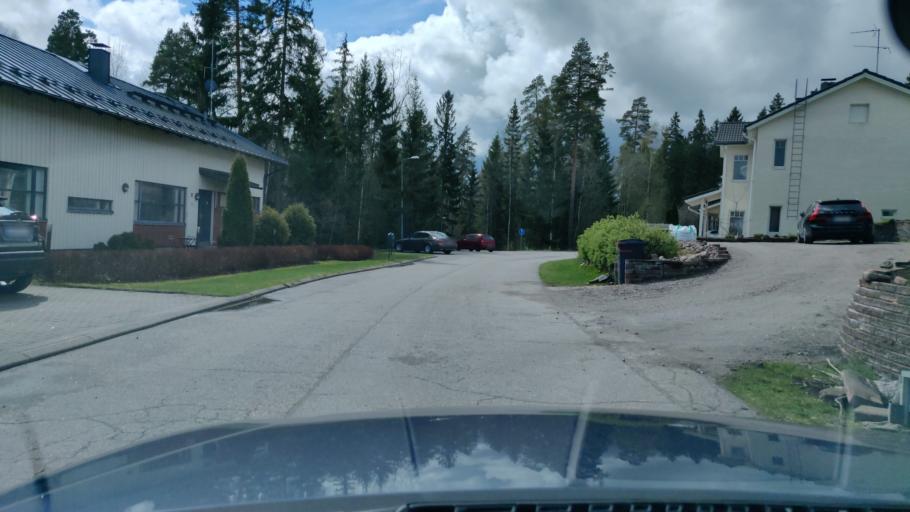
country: FI
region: Uusimaa
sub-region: Helsinki
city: Nurmijaervi
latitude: 60.3621
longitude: 24.7341
